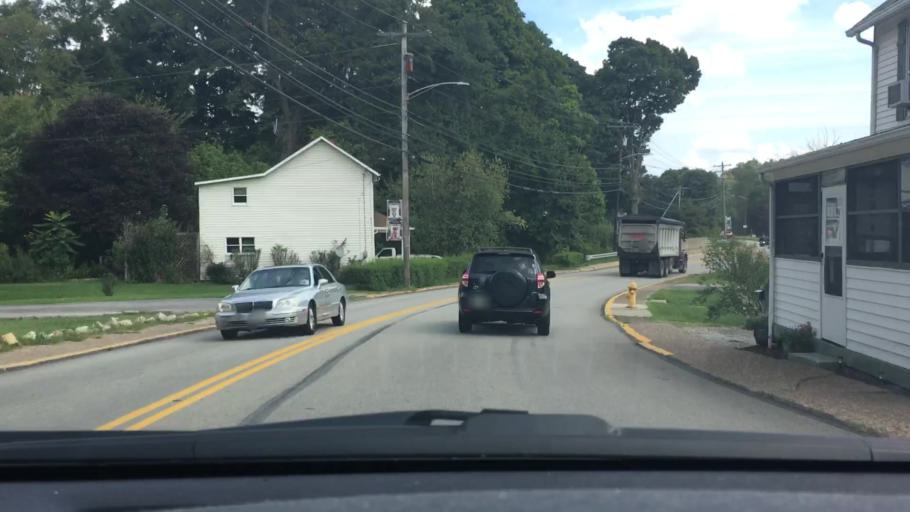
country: US
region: Pennsylvania
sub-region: Washington County
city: Gastonville
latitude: 40.2549
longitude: -79.9975
